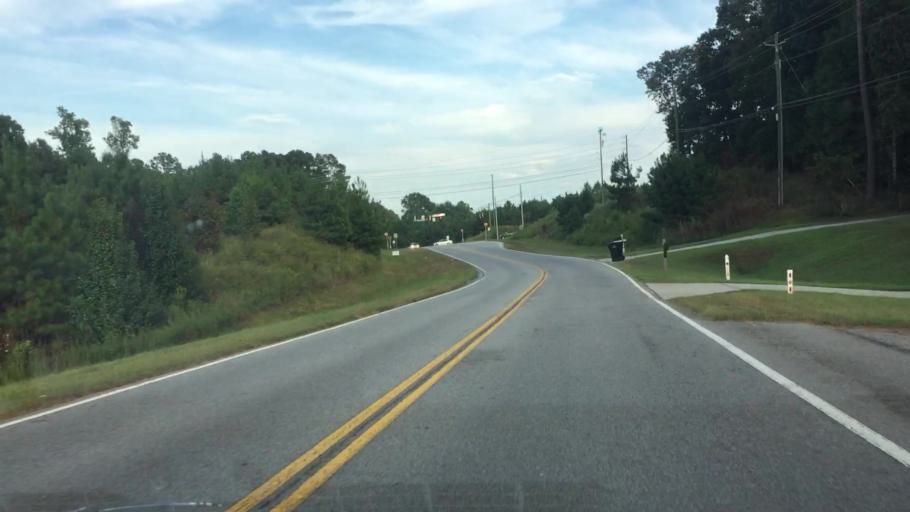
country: US
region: Georgia
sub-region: Henry County
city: McDonough
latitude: 33.5312
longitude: -84.1414
